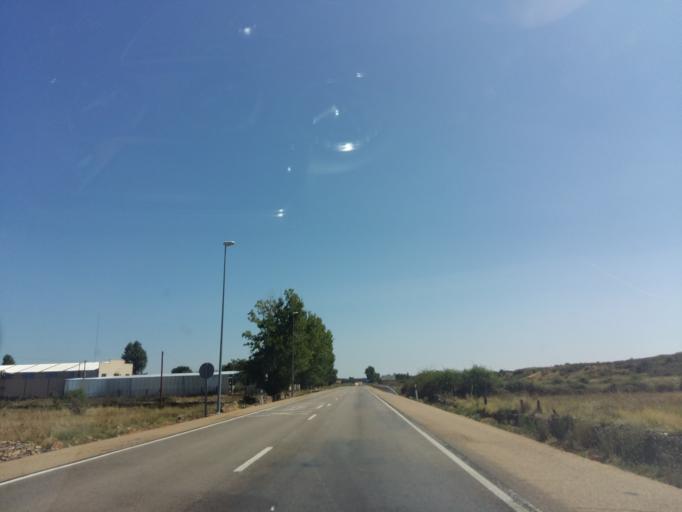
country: ES
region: Castille and Leon
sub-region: Provincia de Leon
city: Astorga
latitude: 42.4456
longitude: -6.0458
